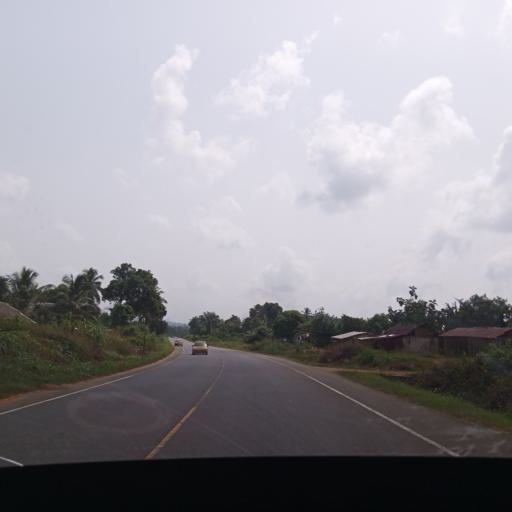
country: LR
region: Margibi
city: Kakata
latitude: 6.2351
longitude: -10.2827
